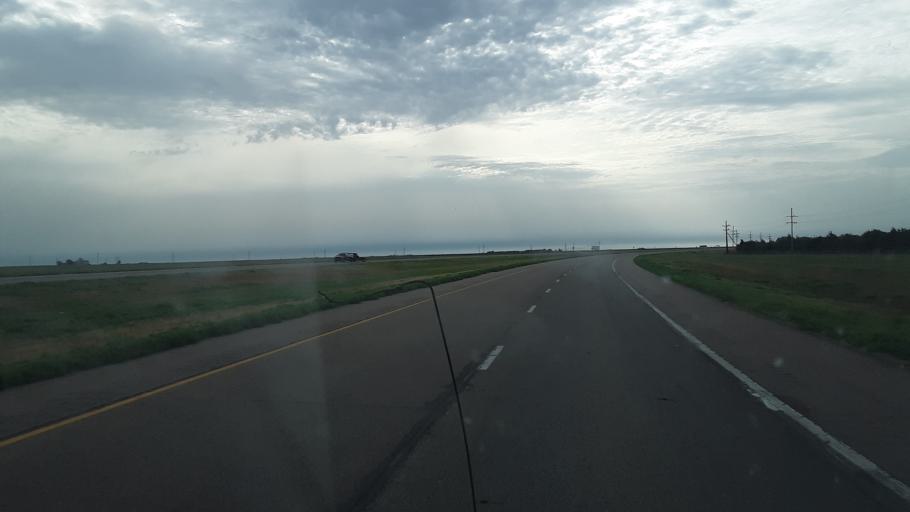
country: US
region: Kansas
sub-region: Finney County
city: Garden City
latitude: 37.9602
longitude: -100.7450
